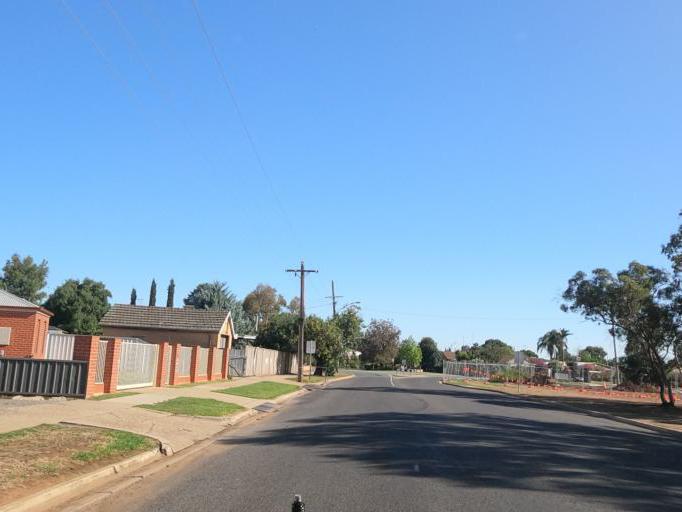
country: AU
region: Victoria
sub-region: Moira
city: Yarrawonga
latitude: -36.0193
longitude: 146.0054
